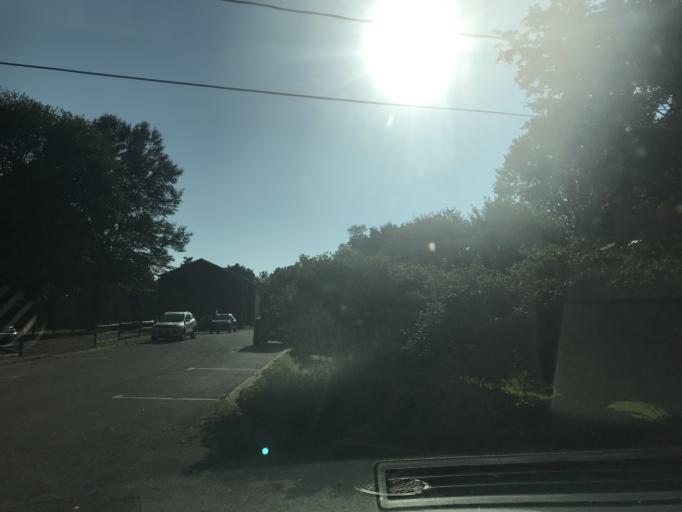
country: US
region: Maryland
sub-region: Harford County
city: Havre de Grace
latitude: 39.5397
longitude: -76.0870
